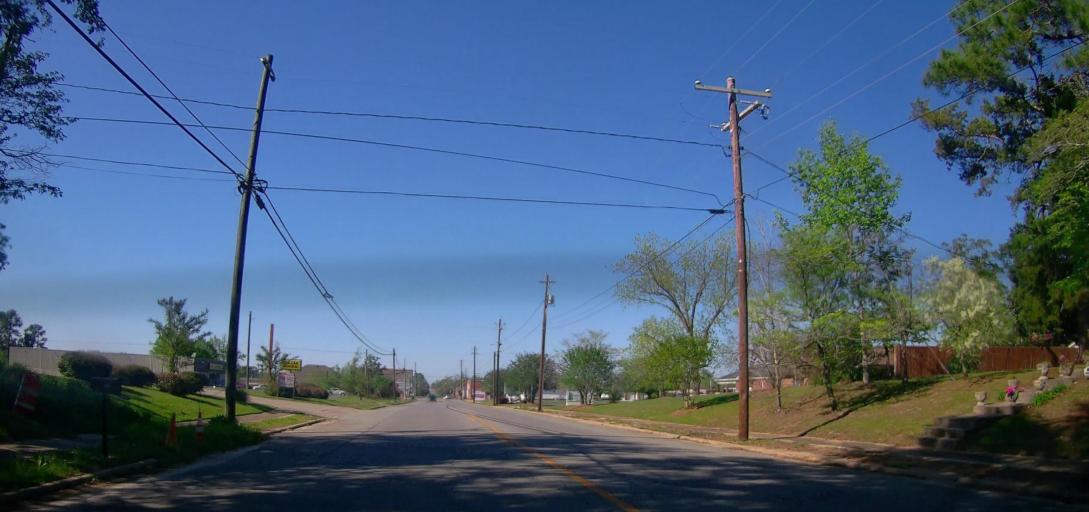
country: US
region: Georgia
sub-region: Wilcox County
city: Rochelle
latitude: 31.9480
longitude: -83.4563
